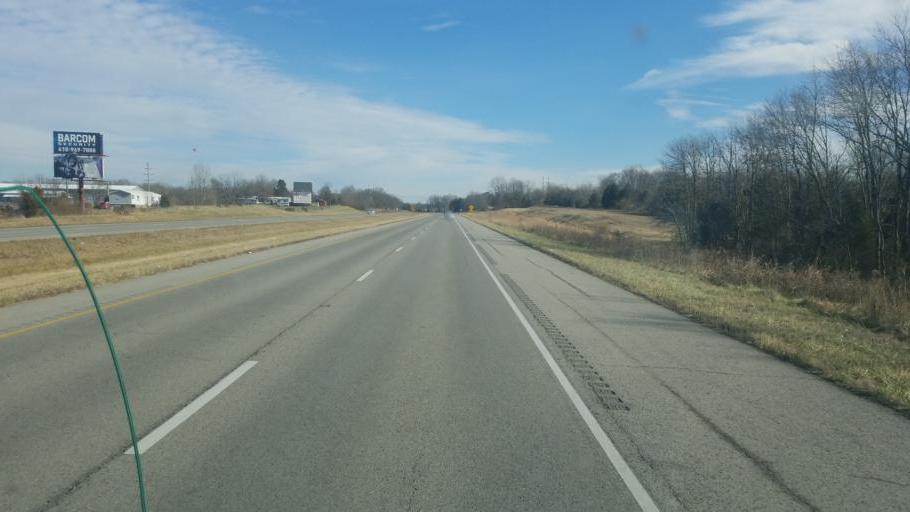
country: US
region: Illinois
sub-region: Williamson County
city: Marion
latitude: 37.7295
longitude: -88.8325
